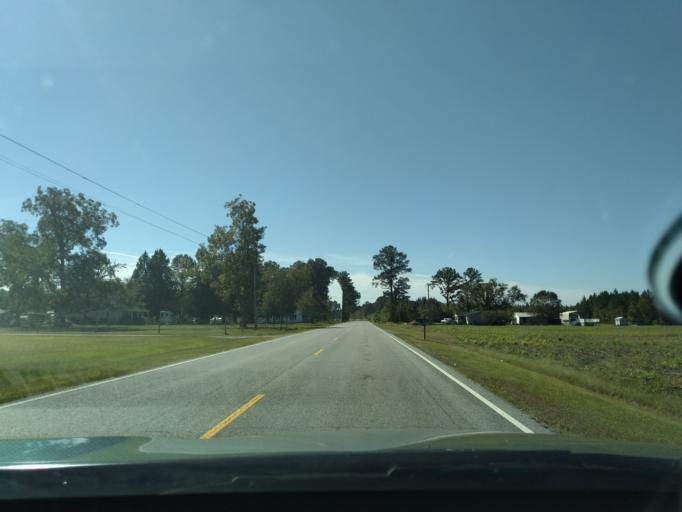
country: US
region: North Carolina
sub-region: Washington County
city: Plymouth
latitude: 35.6719
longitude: -76.7869
